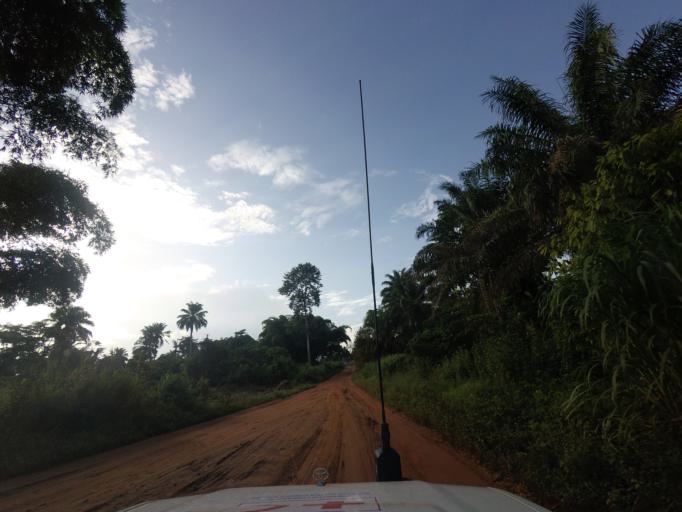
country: GN
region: Nzerekore
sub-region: Nzerekore Prefecture
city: Nzerekore
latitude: 7.6828
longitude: -8.8132
